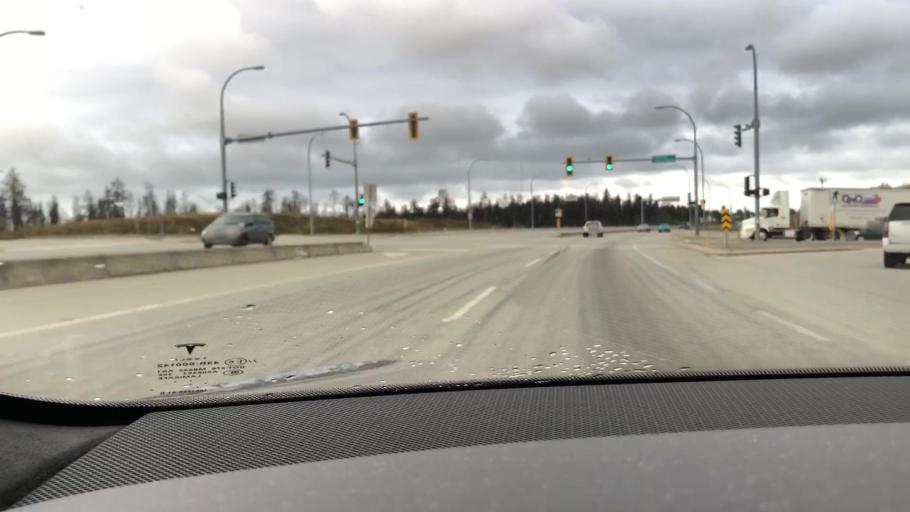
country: CA
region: British Columbia
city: Delta
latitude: 49.1410
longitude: -122.9955
